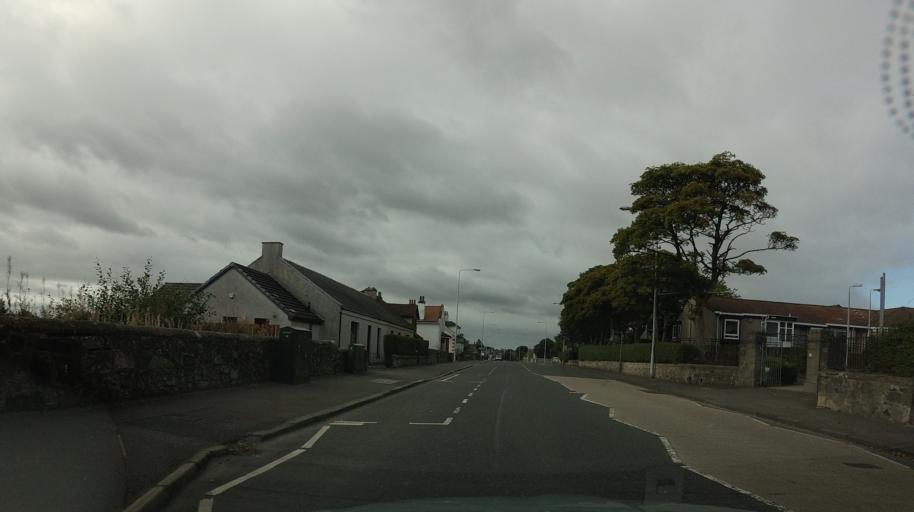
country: GB
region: Scotland
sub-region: Fife
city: Cowdenbeath
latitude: 56.1054
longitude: -3.3473
